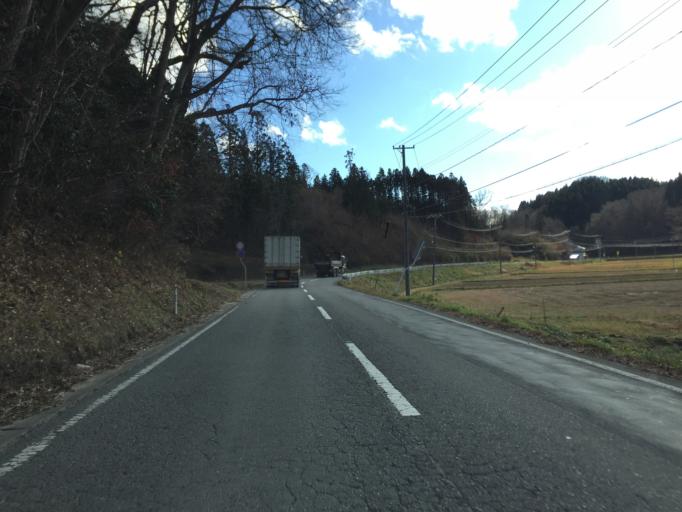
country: JP
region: Fukushima
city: Funehikimachi-funehiki
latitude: 37.5032
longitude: 140.5796
